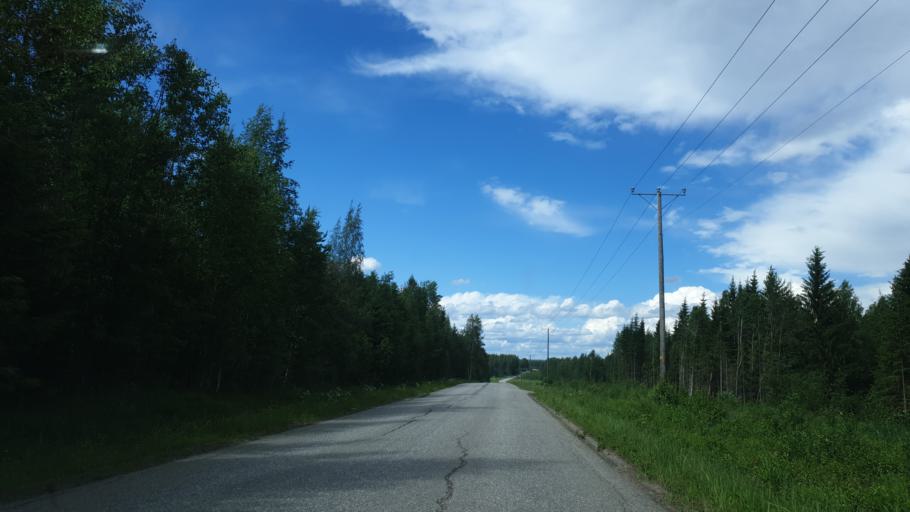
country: FI
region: Northern Savo
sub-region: Koillis-Savo
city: Kaavi
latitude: 62.9811
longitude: 28.7437
